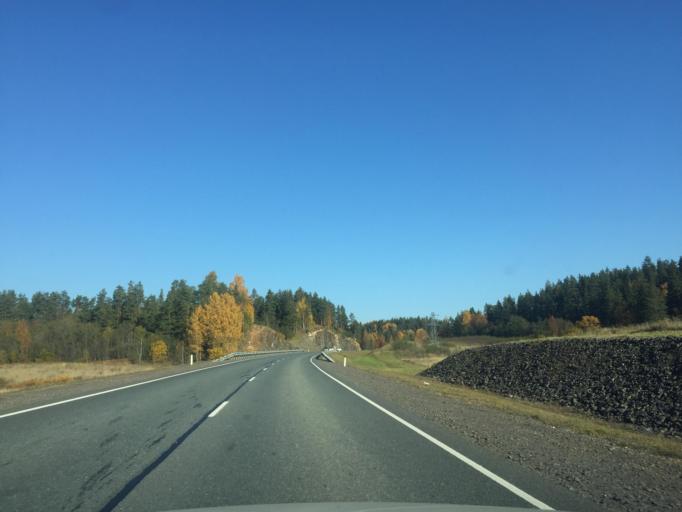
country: RU
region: Leningrad
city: Kuznechnoye
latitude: 61.3080
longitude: 29.7853
